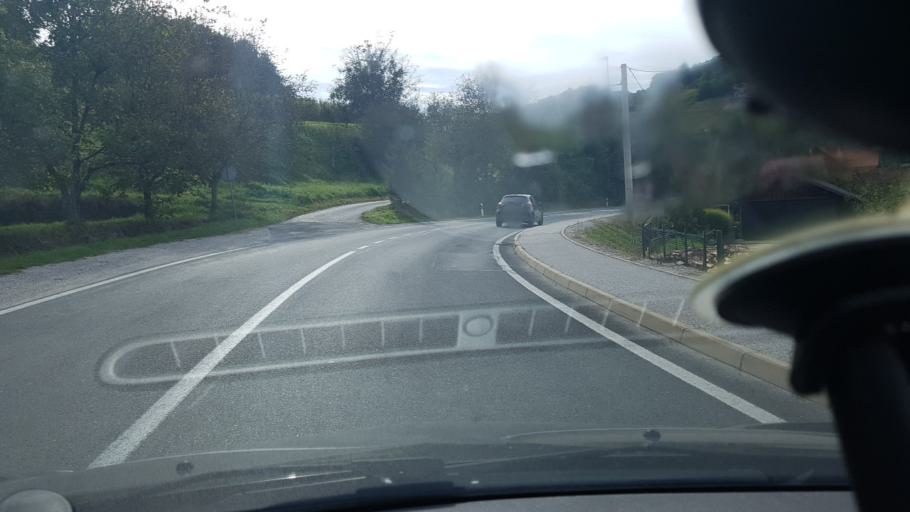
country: HR
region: Varazdinska
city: Lepoglava
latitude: 46.2042
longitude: 16.0261
